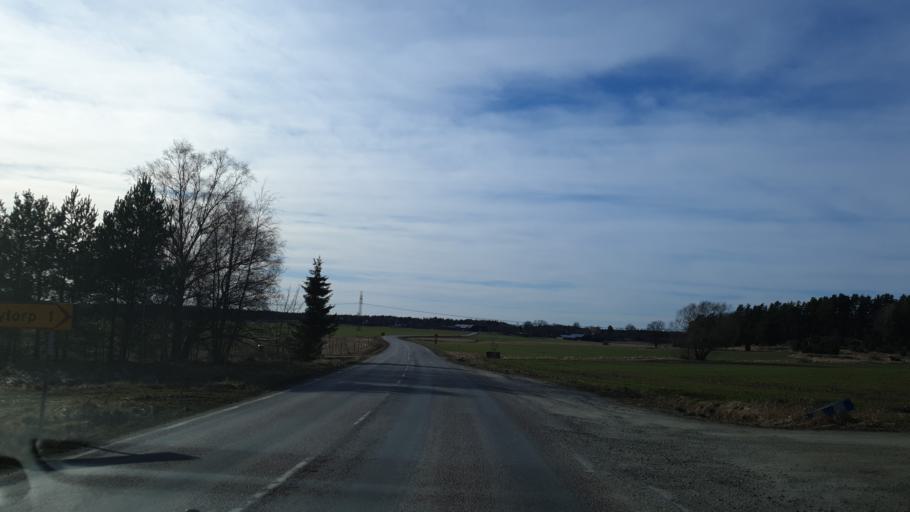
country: SE
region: Uppsala
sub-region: Enkopings Kommun
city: Grillby
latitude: 59.5925
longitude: 17.1979
